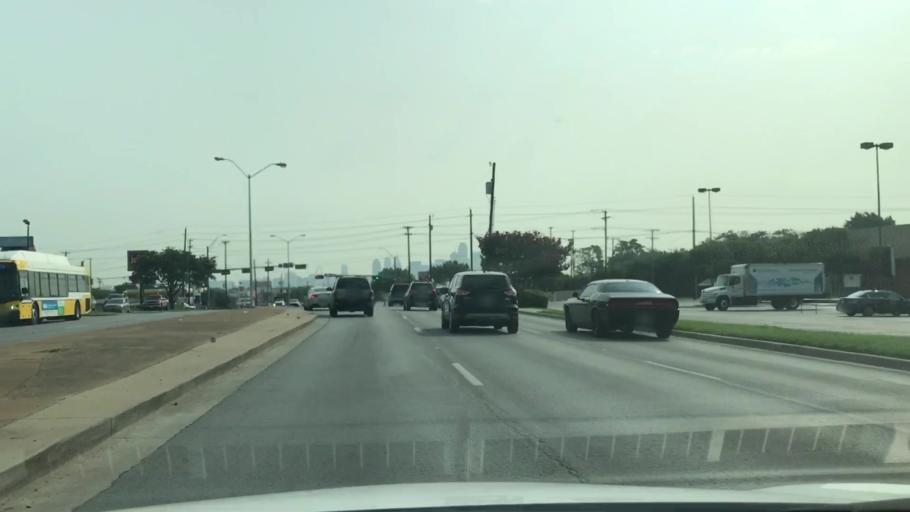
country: US
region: Texas
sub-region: Dallas County
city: Cockrell Hill
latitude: 32.7615
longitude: -96.8580
